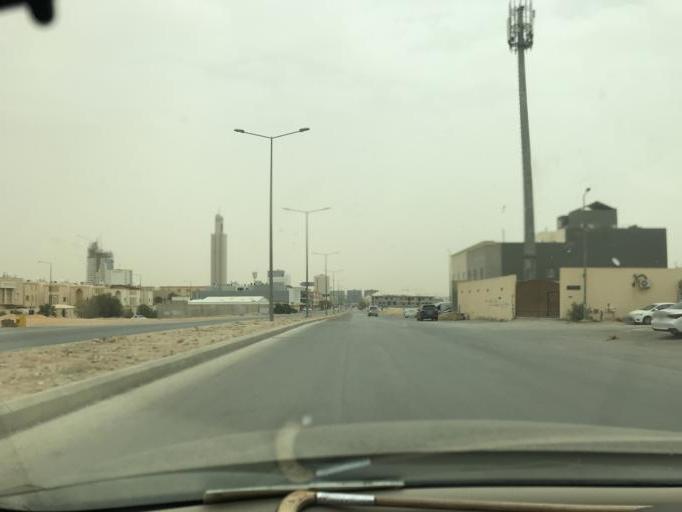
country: SA
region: Ar Riyad
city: Riyadh
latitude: 24.8130
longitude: 46.6077
